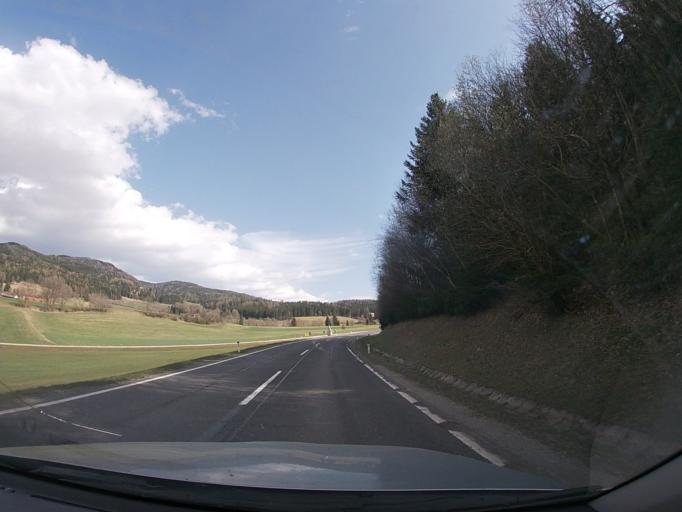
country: AT
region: Styria
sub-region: Politischer Bezirk Murau
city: Perchau am Sattel
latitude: 47.1137
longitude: 14.4565
